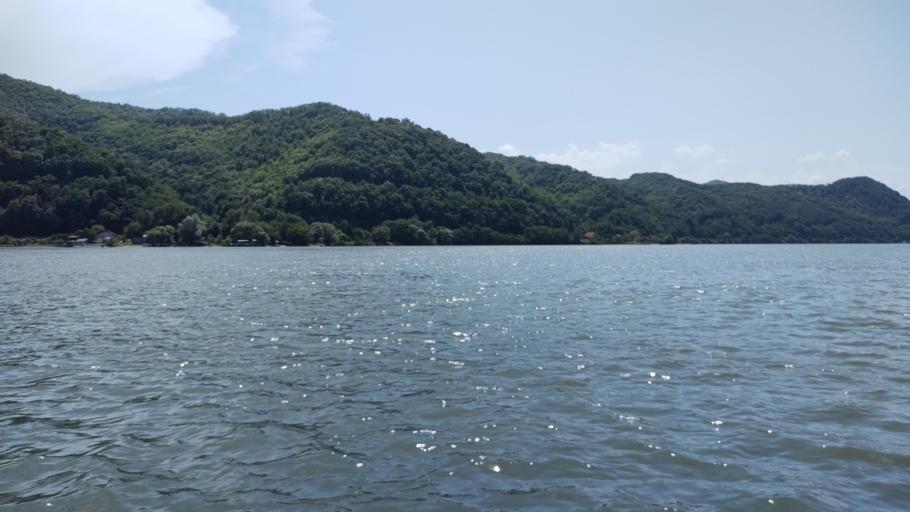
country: RS
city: Radenka
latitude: 44.6583
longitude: 21.7968
